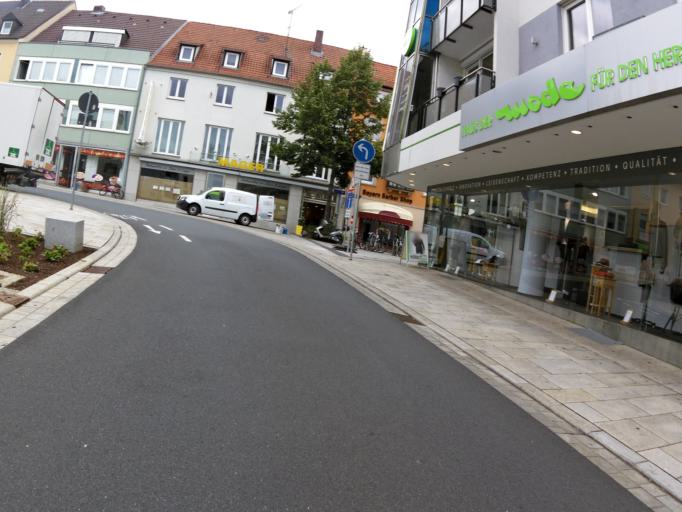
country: DE
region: Bavaria
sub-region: Regierungsbezirk Unterfranken
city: Schweinfurt
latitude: 50.0449
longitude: 10.2287
